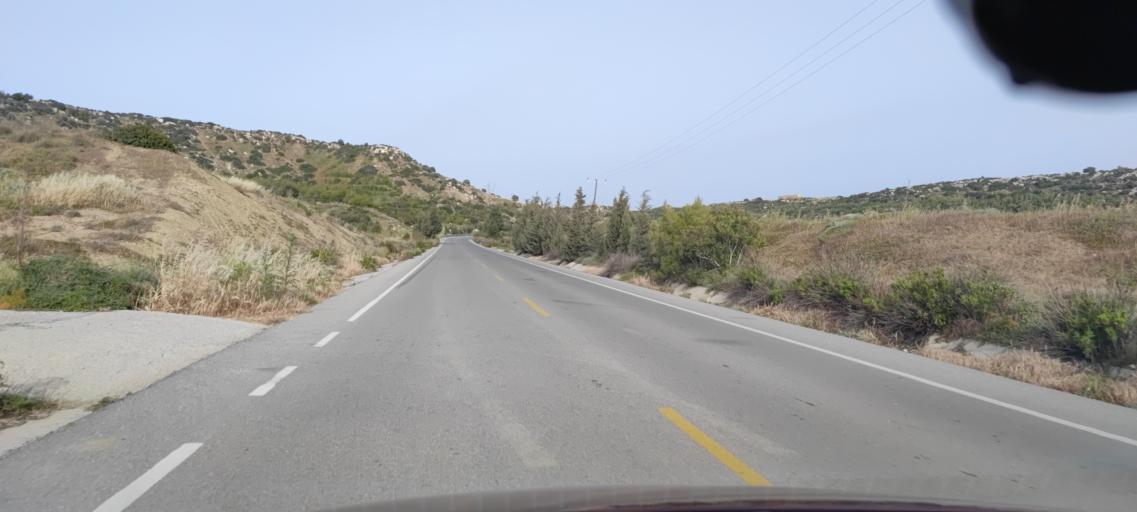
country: CY
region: Ammochostos
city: Leonarisso
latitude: 35.4774
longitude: 34.1306
